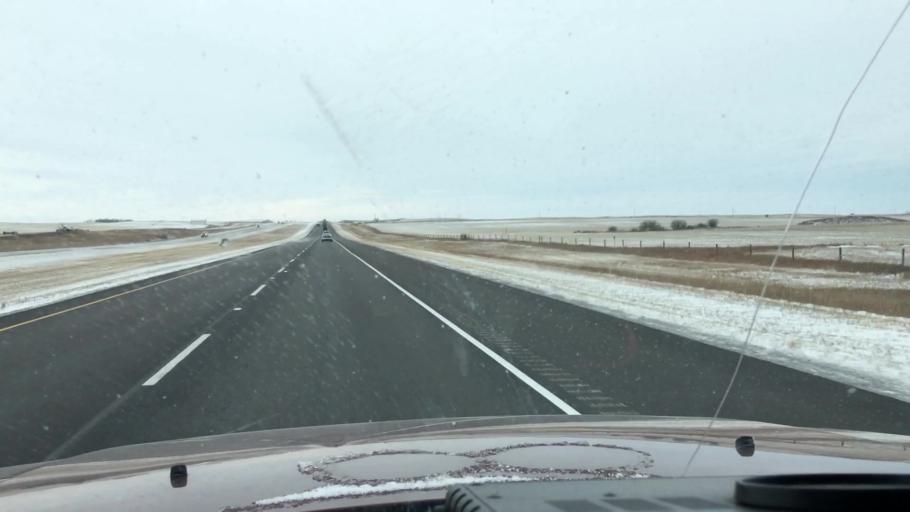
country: CA
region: Saskatchewan
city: Saskatoon
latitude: 51.7150
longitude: -106.4672
